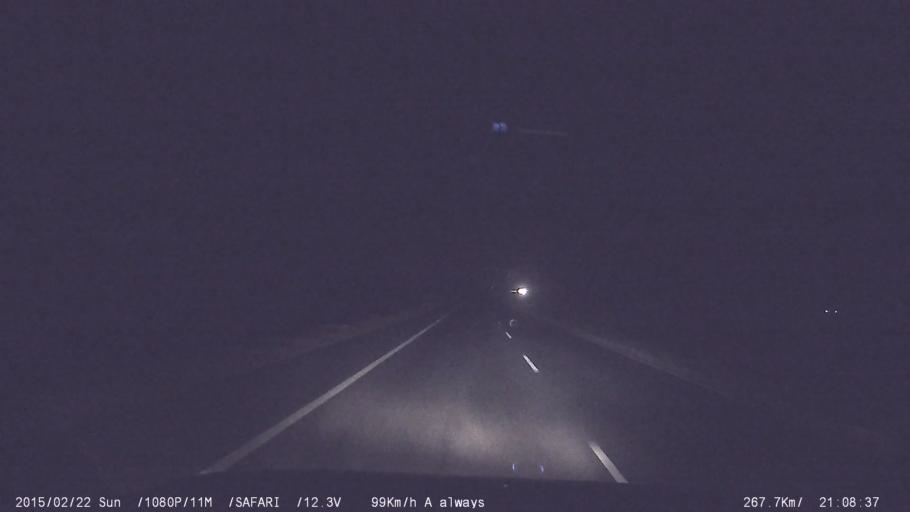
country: IN
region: Tamil Nadu
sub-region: Karur
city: Pallappatti
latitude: 10.7365
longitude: 77.9213
